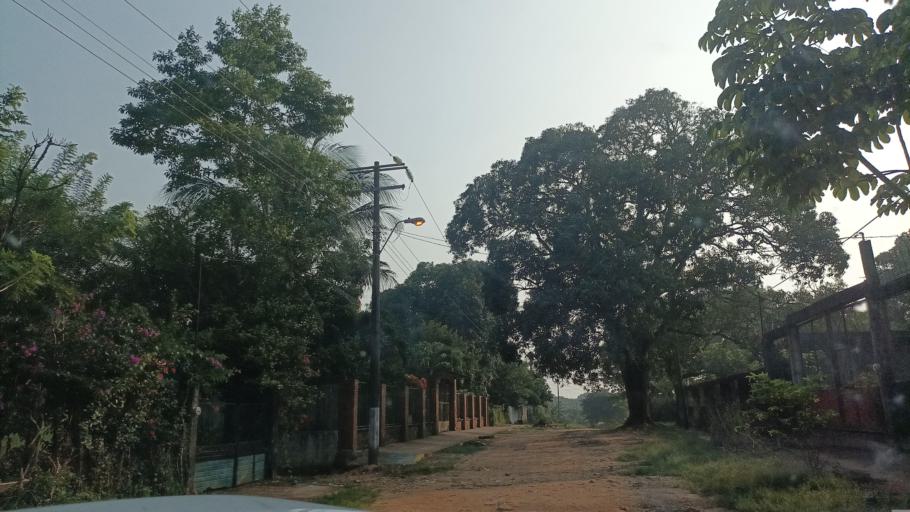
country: MX
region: Veracruz
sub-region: Cosoleacaque
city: Residencial las Olas
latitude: 18.0962
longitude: -94.5713
